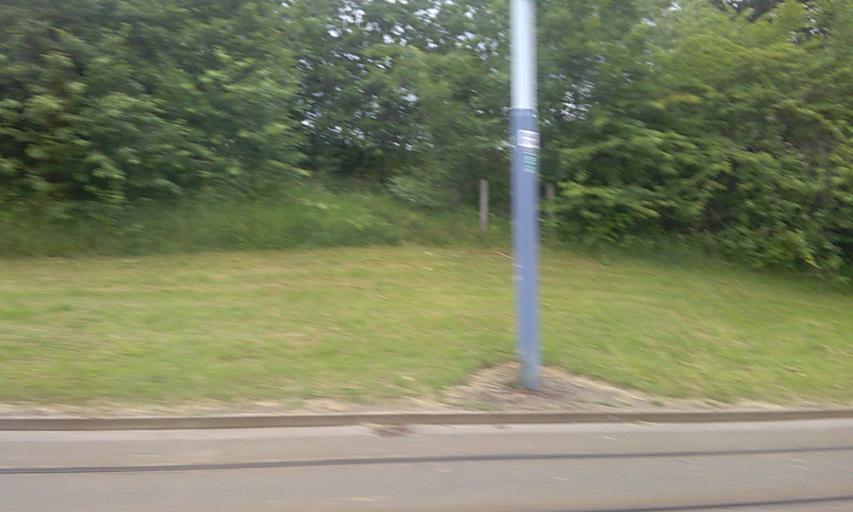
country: GB
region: England
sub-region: Sheffield
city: Sheffield
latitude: 53.3678
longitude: -1.4541
